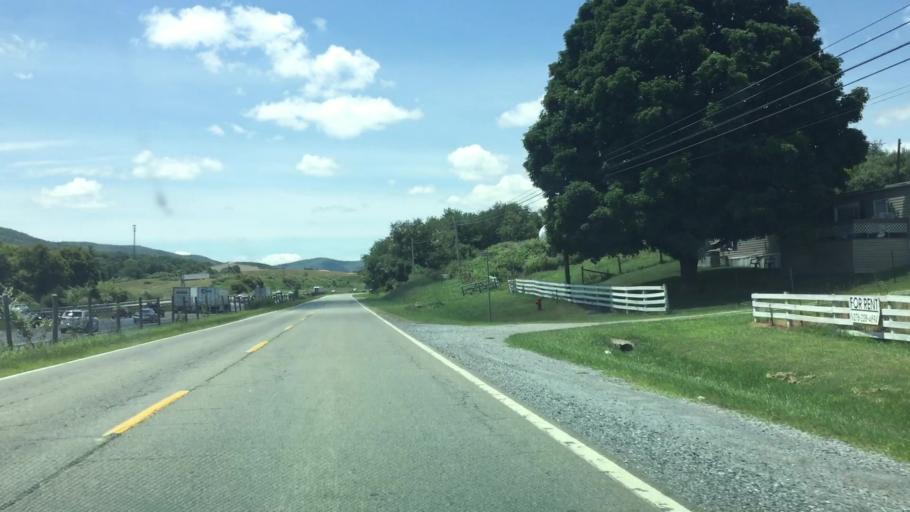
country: US
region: Virginia
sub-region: Wythe County
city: Wytheville
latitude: 36.9398
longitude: -80.9780
